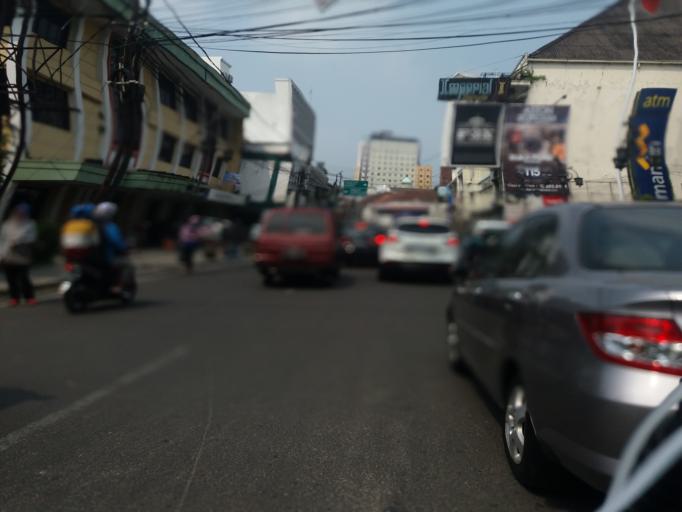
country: ID
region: West Java
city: Bandung
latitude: -6.9152
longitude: 107.6089
